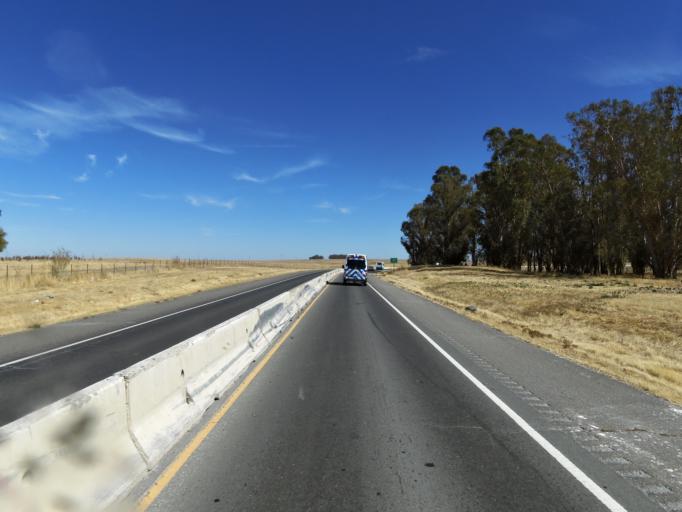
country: US
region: California
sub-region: Solano County
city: Suisun
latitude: 38.2284
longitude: -121.9005
